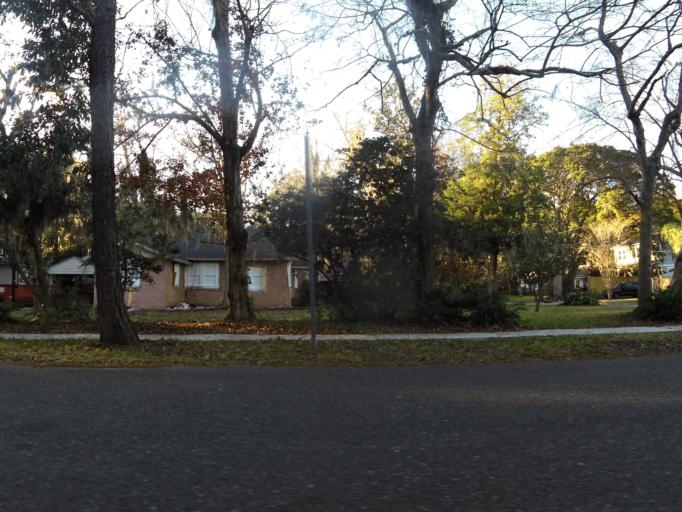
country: US
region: Florida
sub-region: Duval County
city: Jacksonville
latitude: 30.2740
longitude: -81.7034
